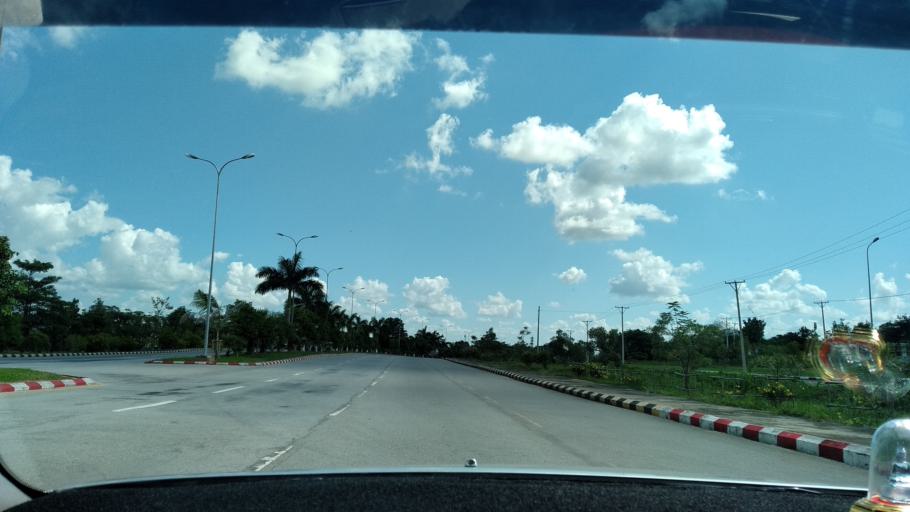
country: MM
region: Mandalay
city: Nay Pyi Taw
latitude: 19.7777
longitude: 96.1429
